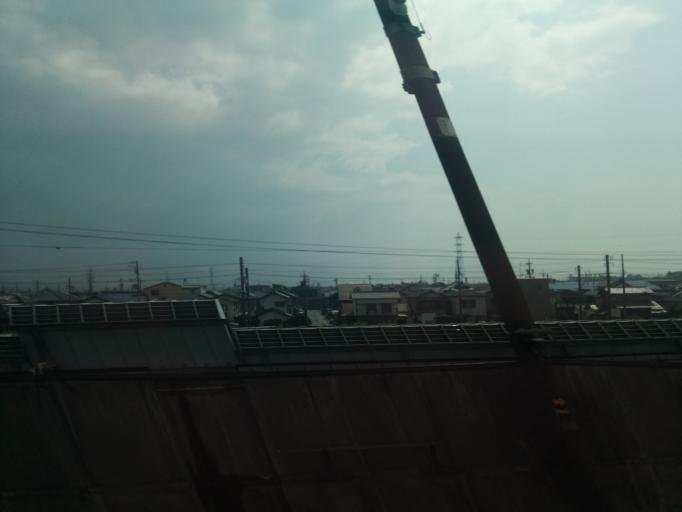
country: JP
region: Shizuoka
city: Shizuoka-shi
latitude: 34.9350
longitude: 138.3630
